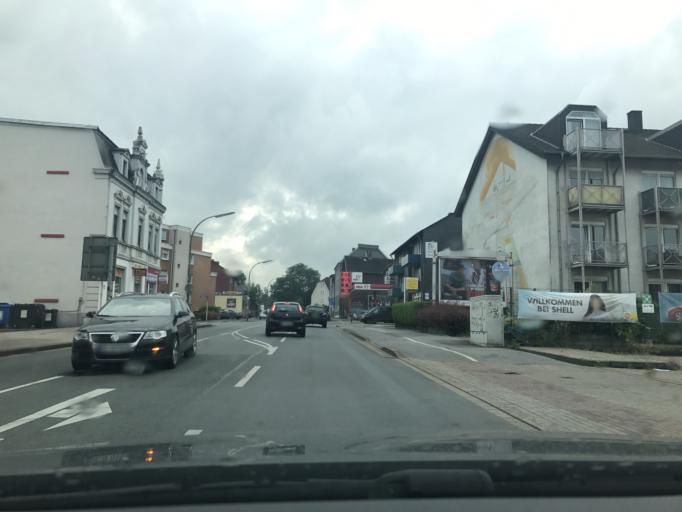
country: DE
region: North Rhine-Westphalia
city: Witten
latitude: 51.4978
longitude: 7.3604
